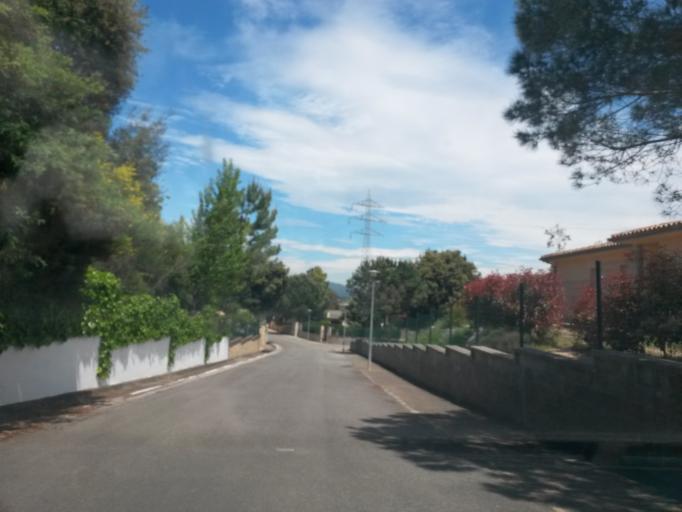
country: ES
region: Catalonia
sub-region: Provincia de Girona
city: Vilablareix
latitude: 41.9653
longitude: 2.7603
